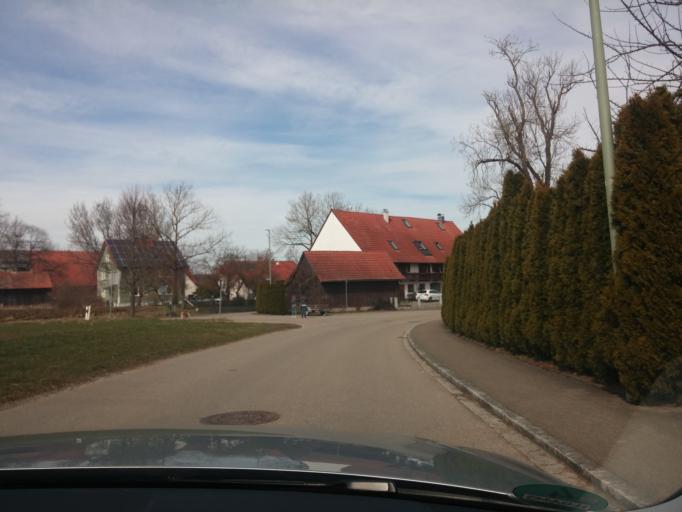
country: DE
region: Bavaria
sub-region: Swabia
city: Memmingen
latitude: 47.9506
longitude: 10.1647
